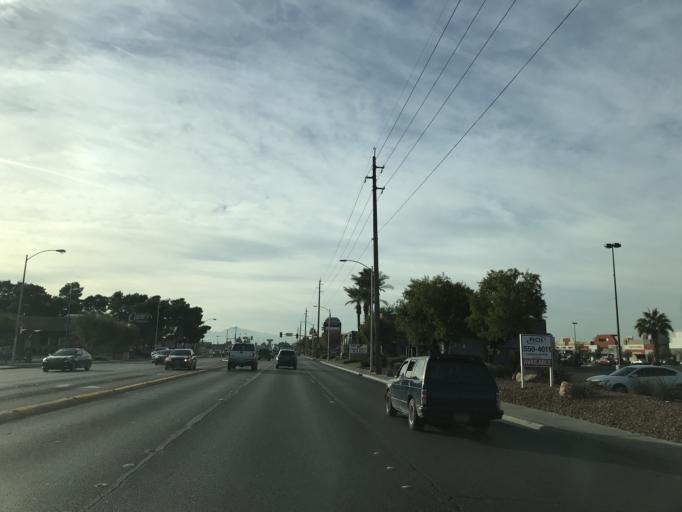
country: US
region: Nevada
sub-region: Clark County
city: Sunrise Manor
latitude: 36.1634
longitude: -115.0623
